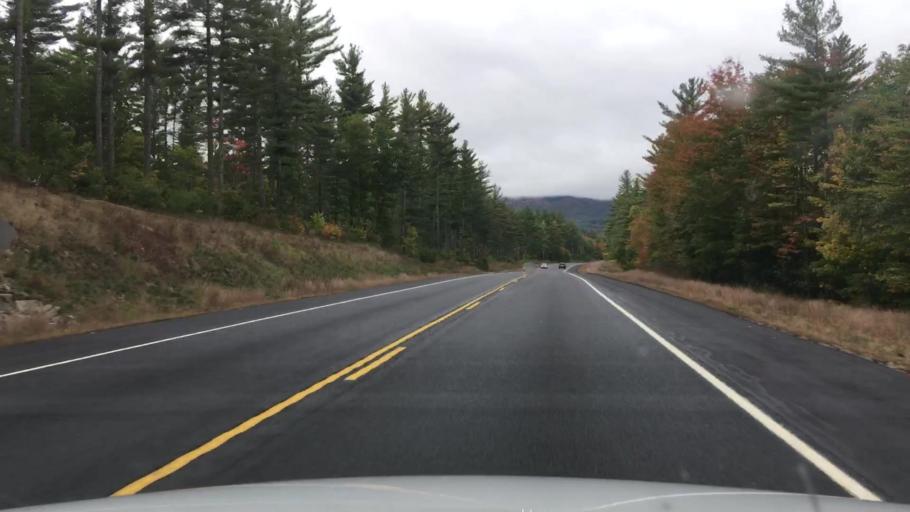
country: US
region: New Hampshire
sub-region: Coos County
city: Gorham
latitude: 44.3940
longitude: -70.9991
